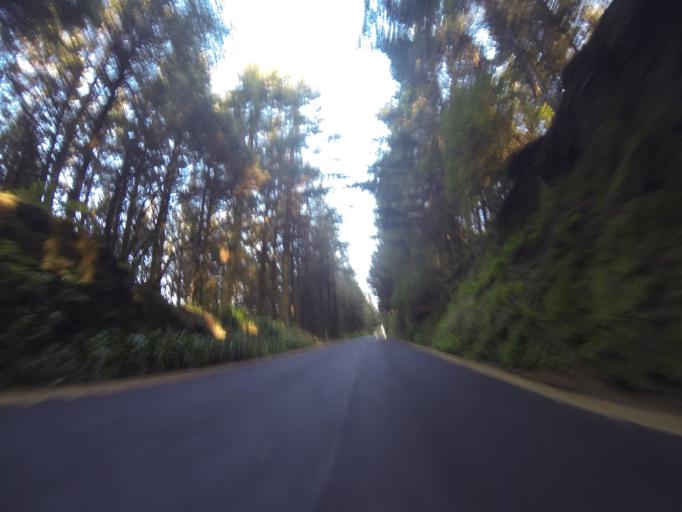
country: PT
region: Madeira
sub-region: Funchal
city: Nossa Senhora do Monte
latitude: 32.7075
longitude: -16.8867
